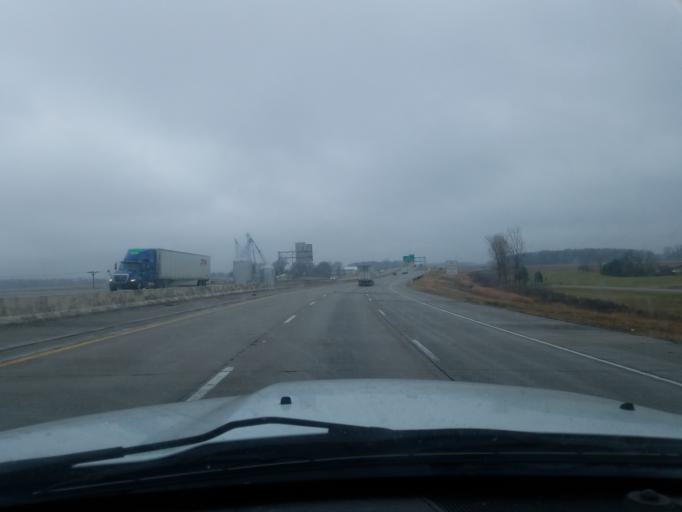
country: US
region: Indiana
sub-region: Huntington County
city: Roanoke
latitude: 40.9610
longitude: -85.2801
